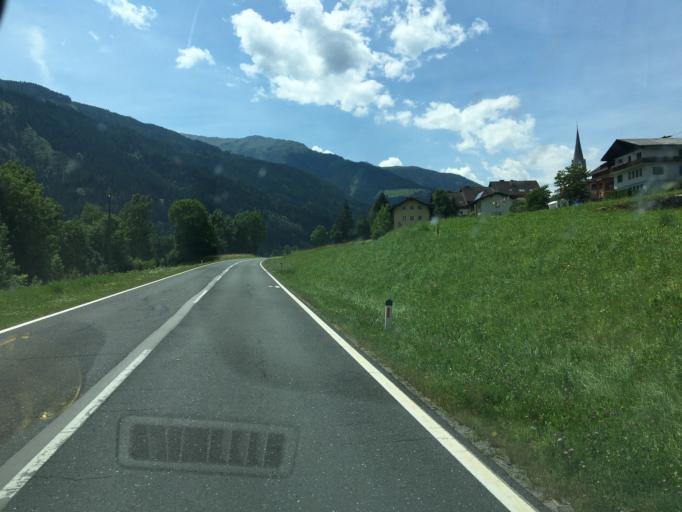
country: AT
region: Carinthia
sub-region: Politischer Bezirk Spittal an der Drau
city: Rangersdorf
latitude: 46.8634
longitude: 12.9677
